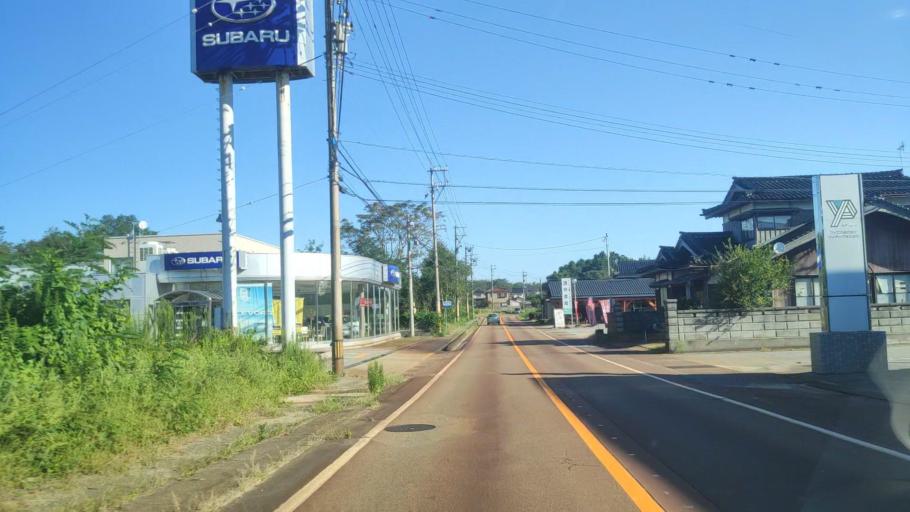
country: JP
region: Ishikawa
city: Hakui
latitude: 36.8739
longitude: 136.7734
